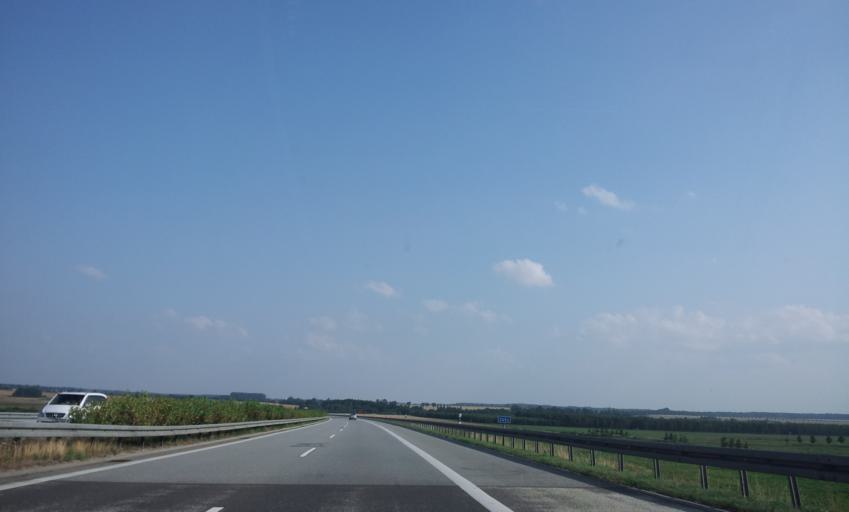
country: DE
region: Mecklenburg-Vorpommern
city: Brunn
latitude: 53.6823
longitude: 13.3302
